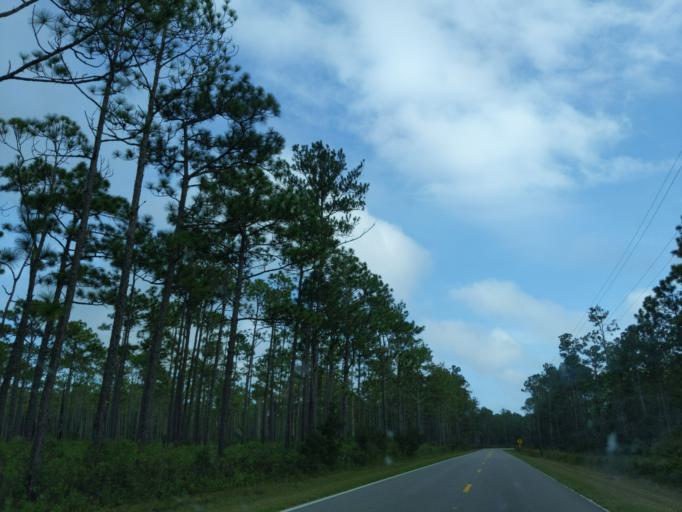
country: US
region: Florida
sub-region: Wakulla County
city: Crawfordville
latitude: 30.1126
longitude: -84.3101
